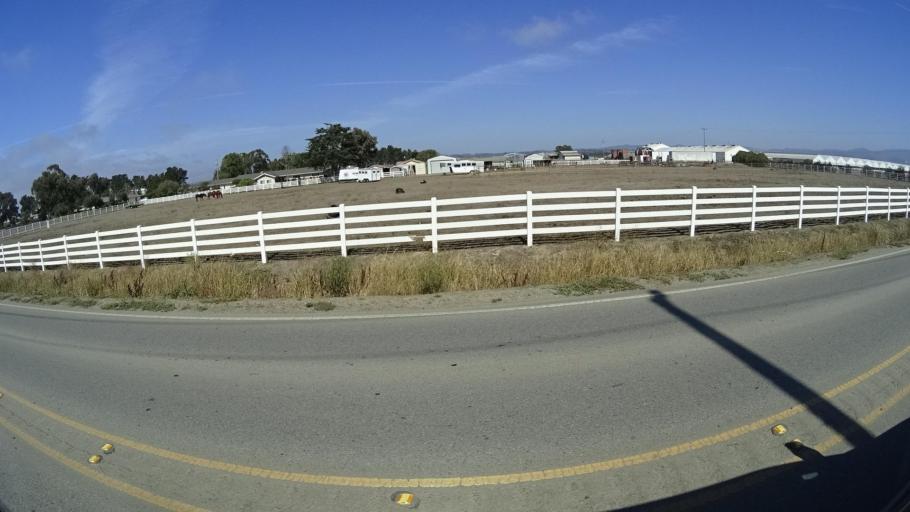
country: US
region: California
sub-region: Monterey County
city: Prunedale
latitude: 36.7433
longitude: -121.6888
